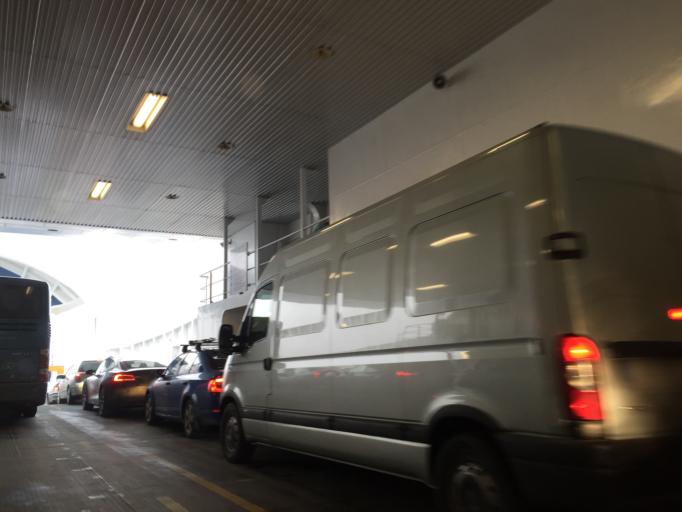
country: EE
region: Saare
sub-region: Orissaare vald
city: Orissaare
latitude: 58.5733
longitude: 23.3949
